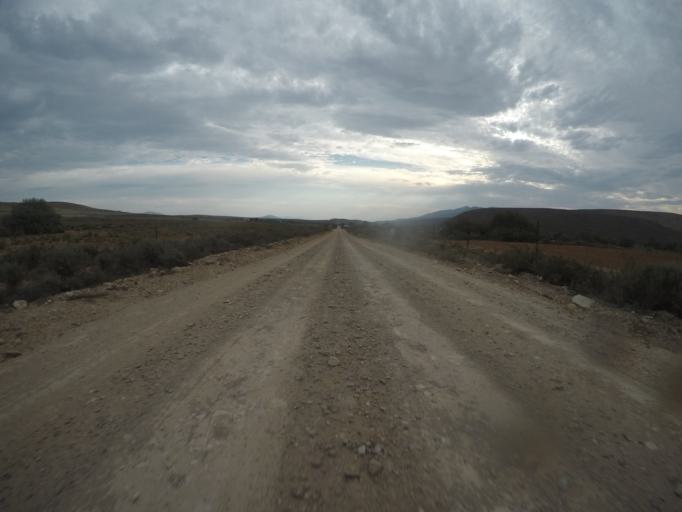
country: ZA
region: Eastern Cape
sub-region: Cacadu District Municipality
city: Willowmore
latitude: -33.4913
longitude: 23.6008
